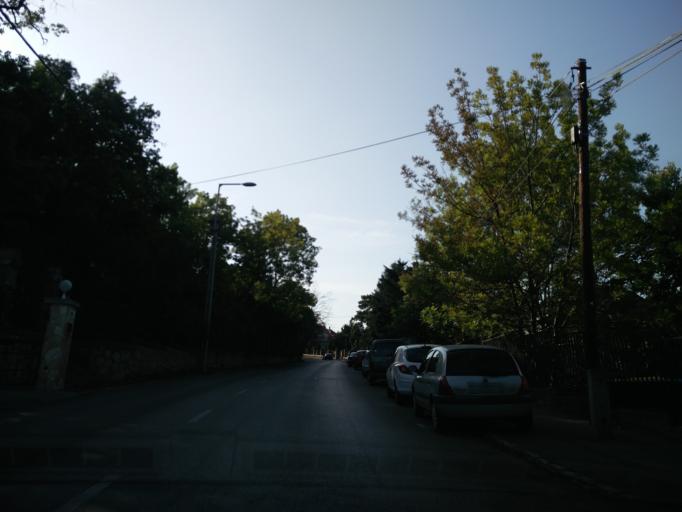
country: HU
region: Budapest
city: Budapest XII. keruelet
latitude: 47.5050
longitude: 18.9970
